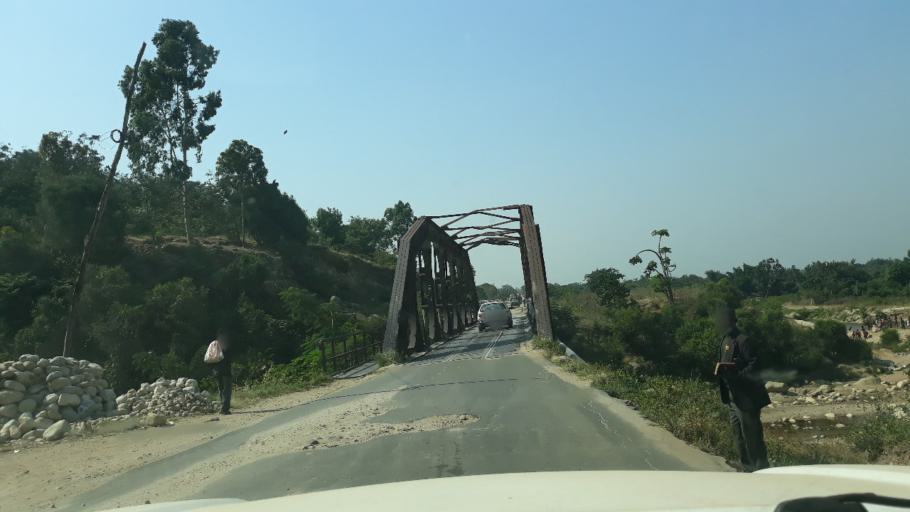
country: CD
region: South Kivu
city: Uvira
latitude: -3.2413
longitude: 29.1607
